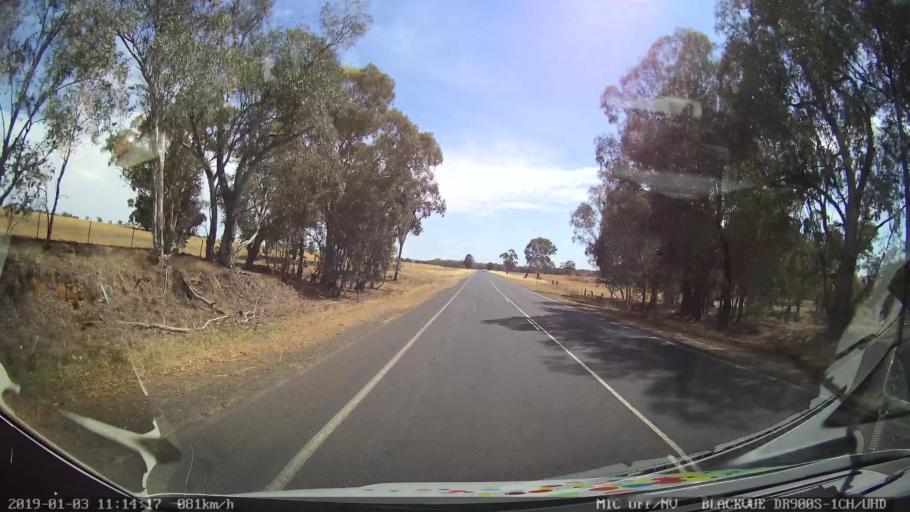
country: AU
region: New South Wales
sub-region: Young
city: Young
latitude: -34.1779
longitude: 148.2606
